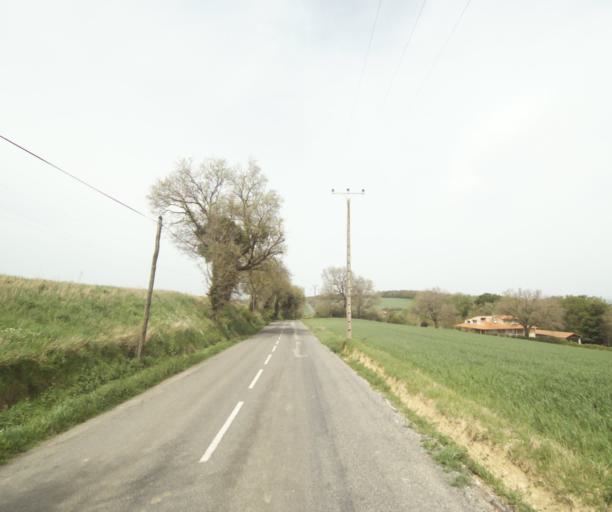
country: FR
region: Midi-Pyrenees
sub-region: Departement de la Haute-Garonne
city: Pechabou
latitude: 43.4925
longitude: 1.4929
